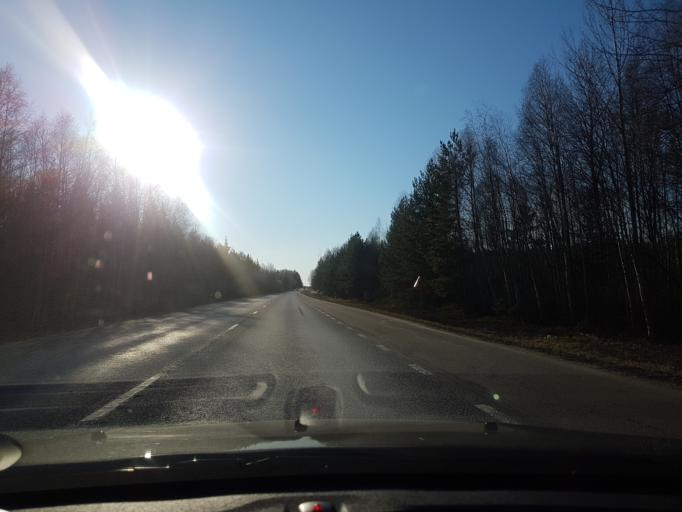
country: SE
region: Uppsala
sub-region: Heby Kommun
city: Morgongava
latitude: 59.8959
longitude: 17.1193
